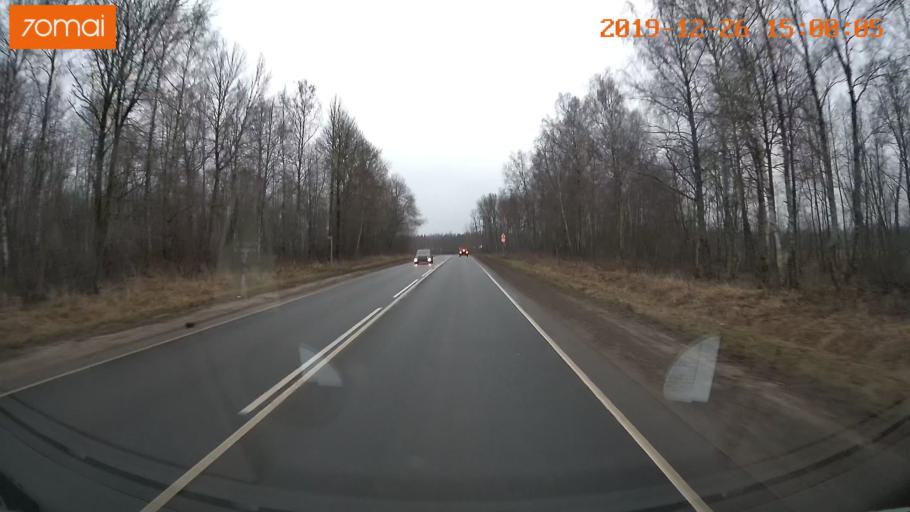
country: RU
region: Jaroslavl
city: Rybinsk
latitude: 58.2500
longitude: 38.8491
